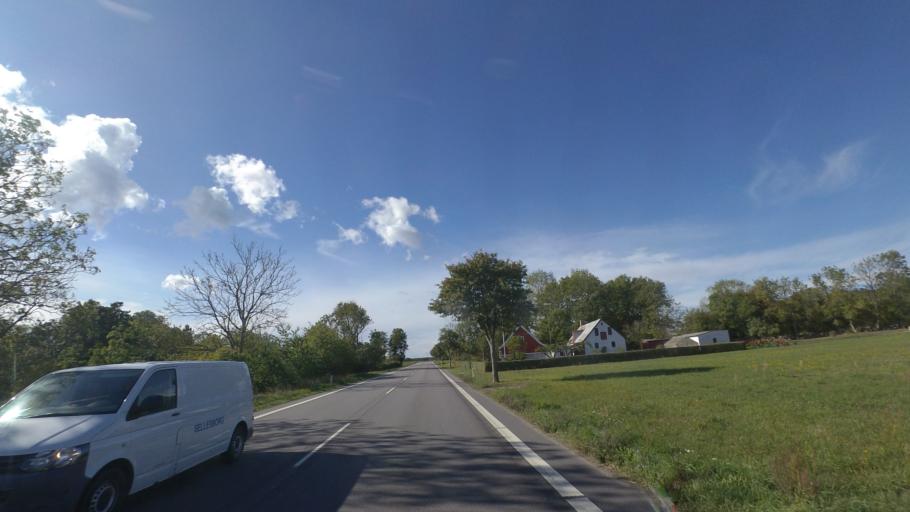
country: DK
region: Capital Region
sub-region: Bornholm Kommune
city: Ronne
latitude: 55.0745
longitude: 14.7871
